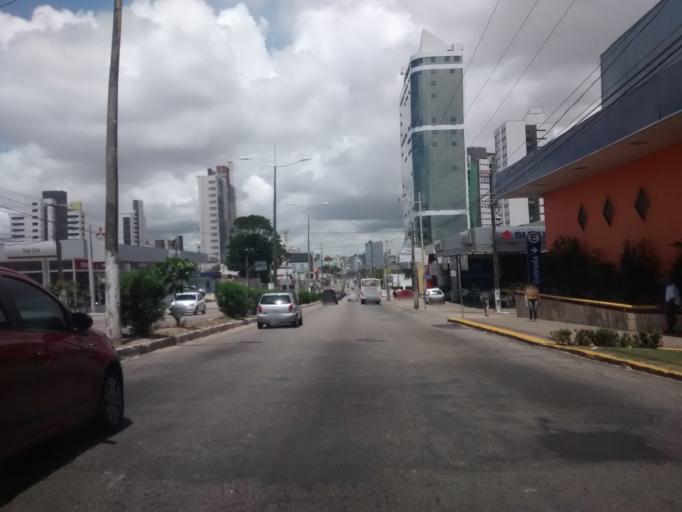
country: BR
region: Rio Grande do Norte
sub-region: Natal
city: Natal
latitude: -5.8160
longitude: -35.2064
